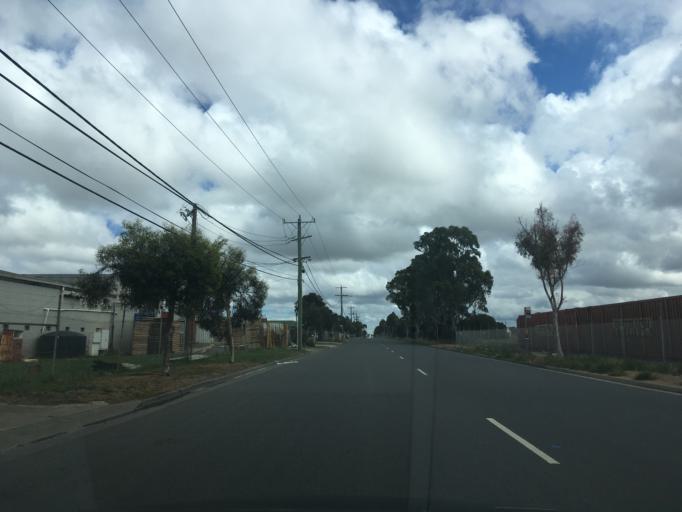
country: AU
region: Victoria
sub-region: Brimbank
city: Brooklyn
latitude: -37.8340
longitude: 144.8034
